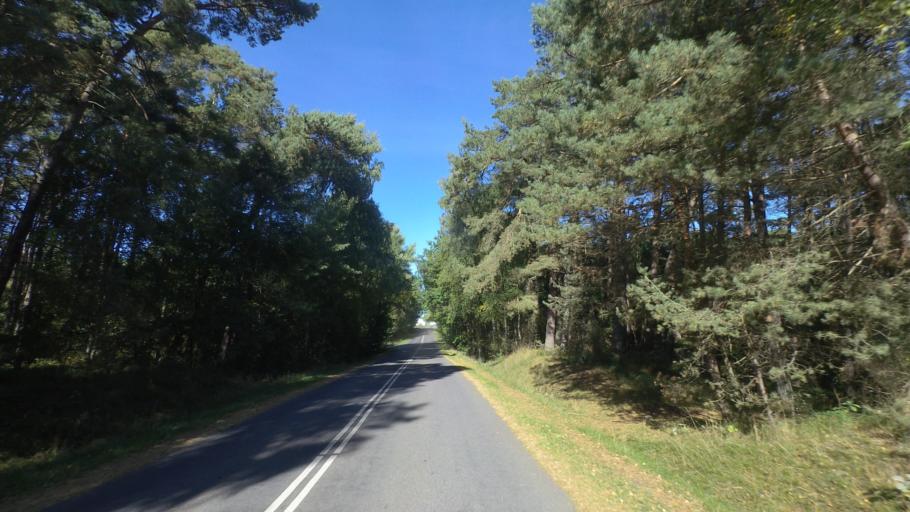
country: DK
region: Capital Region
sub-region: Bornholm Kommune
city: Nexo
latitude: 54.9999
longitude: 15.0755
